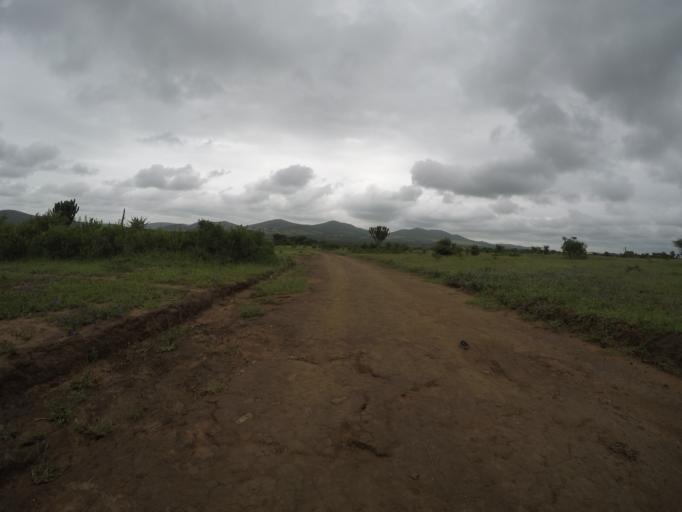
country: ZA
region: KwaZulu-Natal
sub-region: uThungulu District Municipality
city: Empangeni
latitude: -28.6042
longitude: 31.8644
